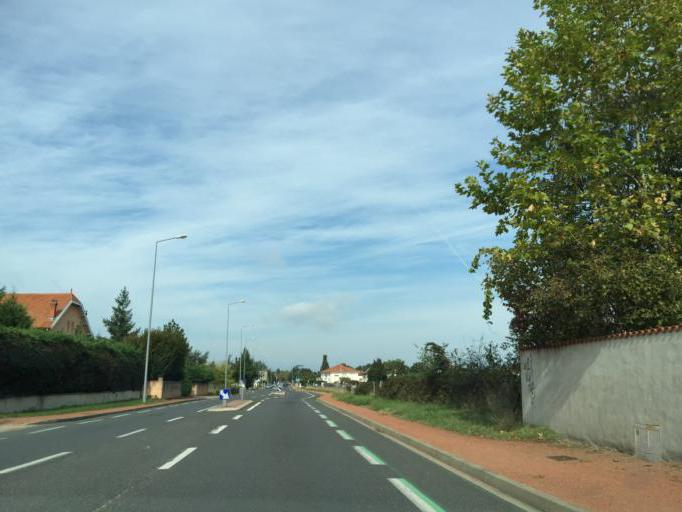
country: FR
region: Rhone-Alpes
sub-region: Departement de la Loire
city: Bonson
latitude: 45.5272
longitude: 4.2072
